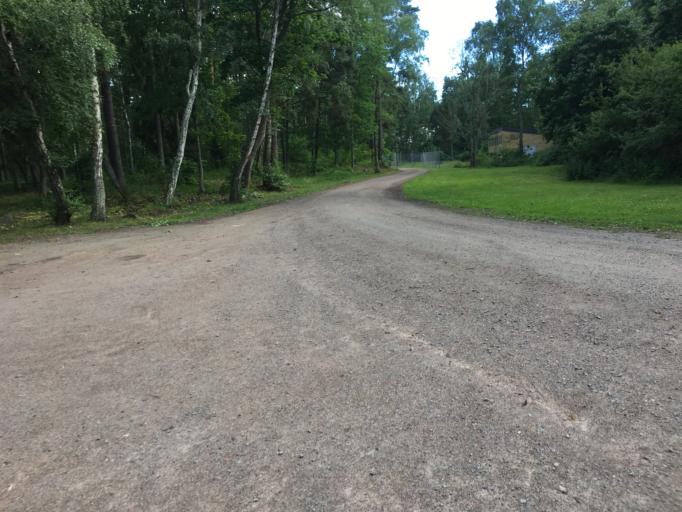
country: SE
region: Kalmar
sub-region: Kalmar Kommun
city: Kalmar
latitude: 56.6557
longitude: 16.3227
